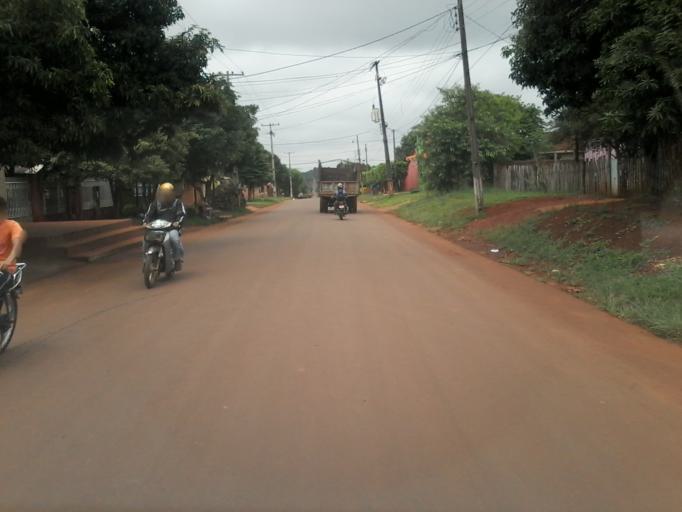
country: PY
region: Alto Parana
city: Ciudad del Este
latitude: -25.4074
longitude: -54.6450
